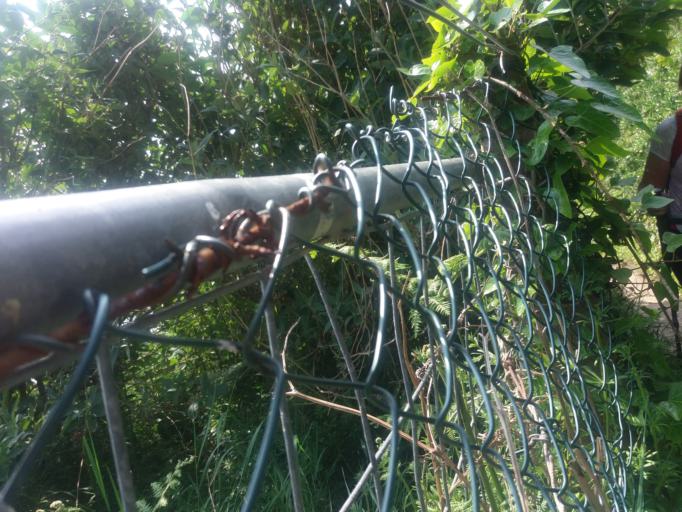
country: IE
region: Leinster
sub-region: Fingal County
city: Howth
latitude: 53.3651
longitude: -6.0645
